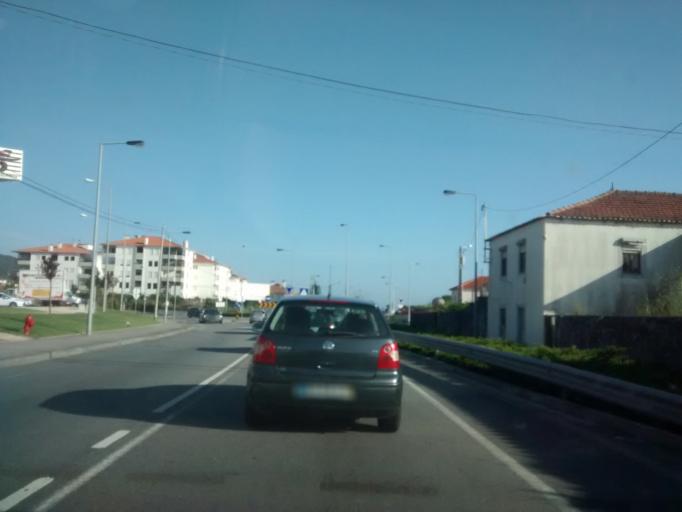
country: PT
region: Viana do Castelo
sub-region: Viana do Castelo
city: Areosa
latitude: 41.7246
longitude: -8.8598
